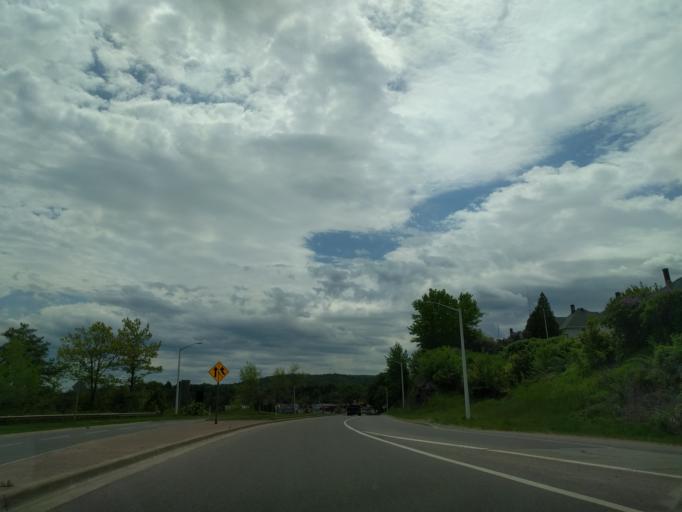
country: US
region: Michigan
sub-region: Marquette County
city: Marquette
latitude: 46.5372
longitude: -87.3954
